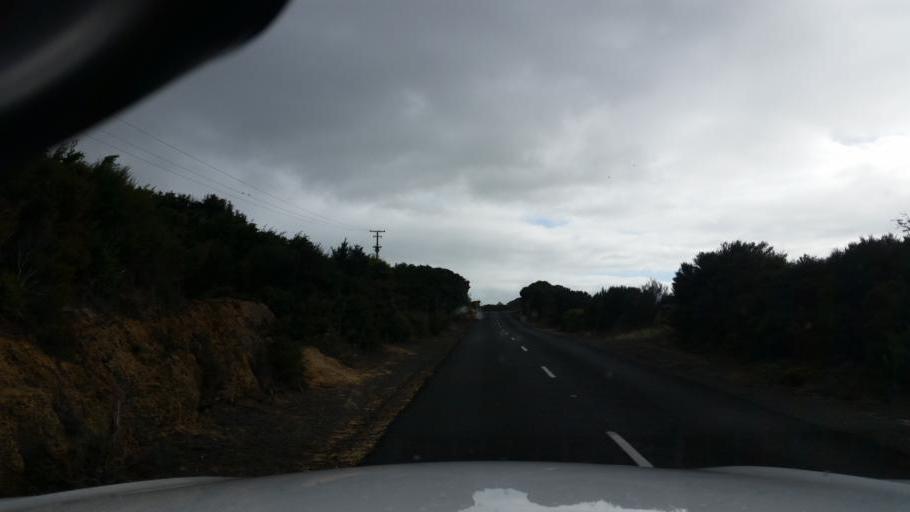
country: NZ
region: Northland
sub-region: Kaipara District
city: Dargaville
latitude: -35.8234
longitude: 173.6501
